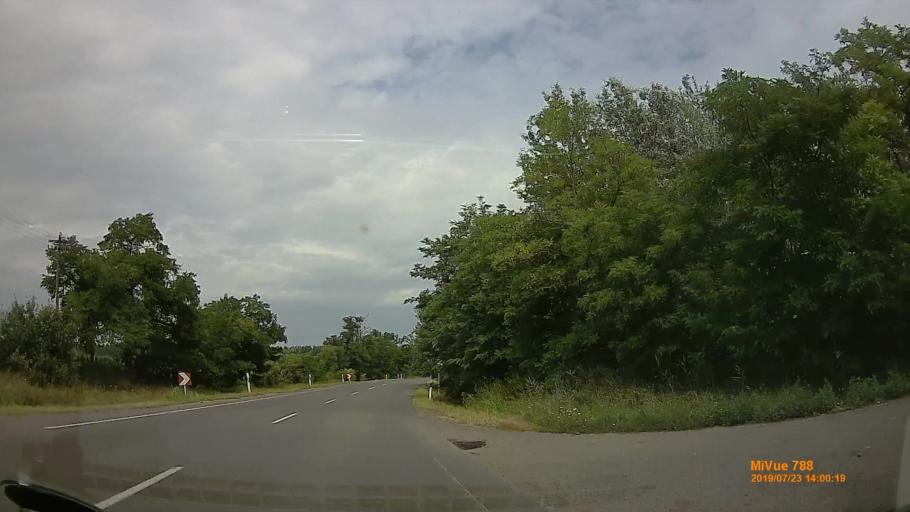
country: HU
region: Szabolcs-Szatmar-Bereg
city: Tiszavasvari
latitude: 47.9359
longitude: 21.3042
